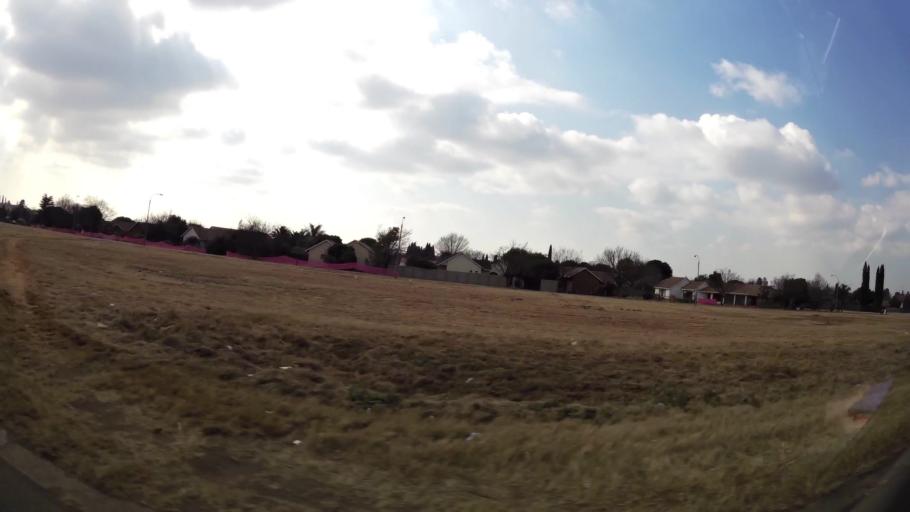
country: ZA
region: Gauteng
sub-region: Ekurhuleni Metropolitan Municipality
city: Benoni
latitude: -26.1628
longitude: 28.2780
